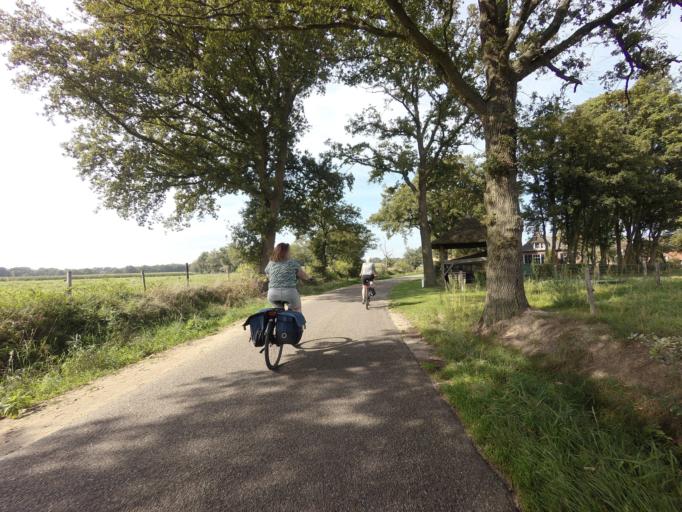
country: NL
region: Overijssel
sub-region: Gemeente Hof van Twente
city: Markelo
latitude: 52.2625
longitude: 6.5202
